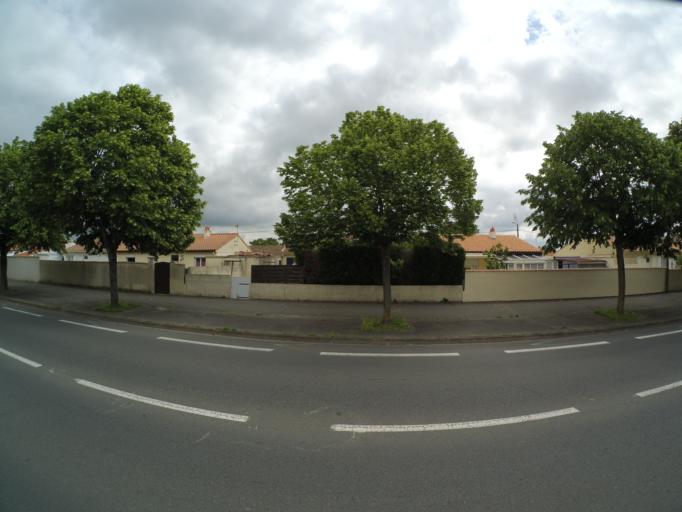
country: FR
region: Poitou-Charentes
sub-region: Departement de la Charente-Maritime
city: Rochefort
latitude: 45.9568
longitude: -0.9693
